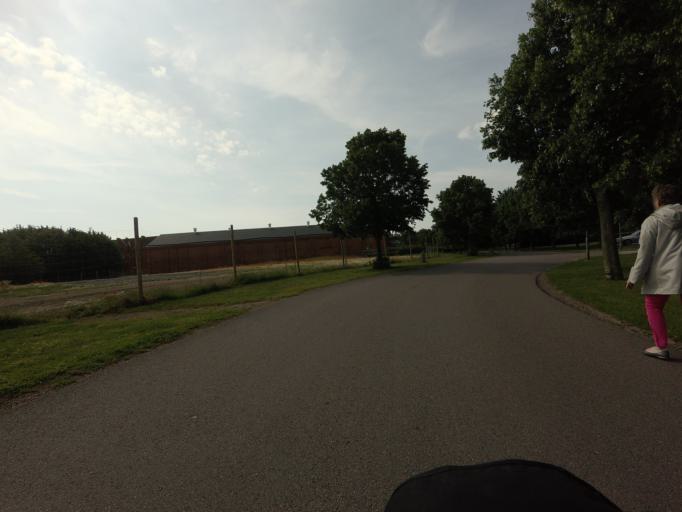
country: SE
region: Skane
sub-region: Malmo
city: Tygelsjo
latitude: 55.4977
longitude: 13.0031
